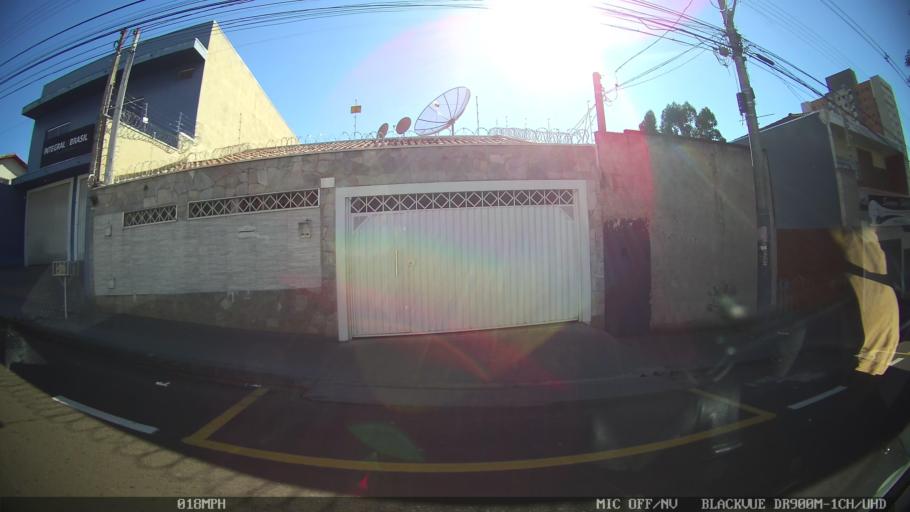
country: BR
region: Sao Paulo
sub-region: Franca
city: Franca
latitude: -20.5299
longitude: -47.4068
